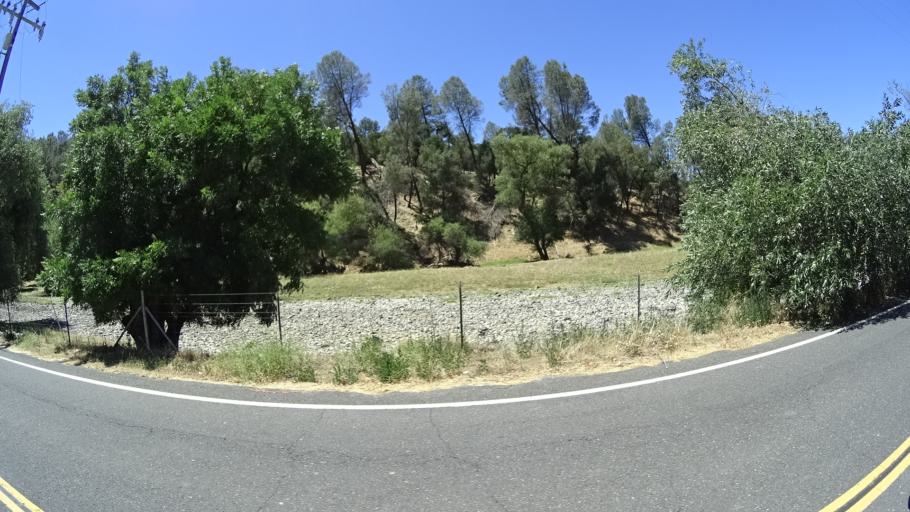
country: US
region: California
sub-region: Calaveras County
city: San Andreas
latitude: 38.1412
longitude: -120.6622
